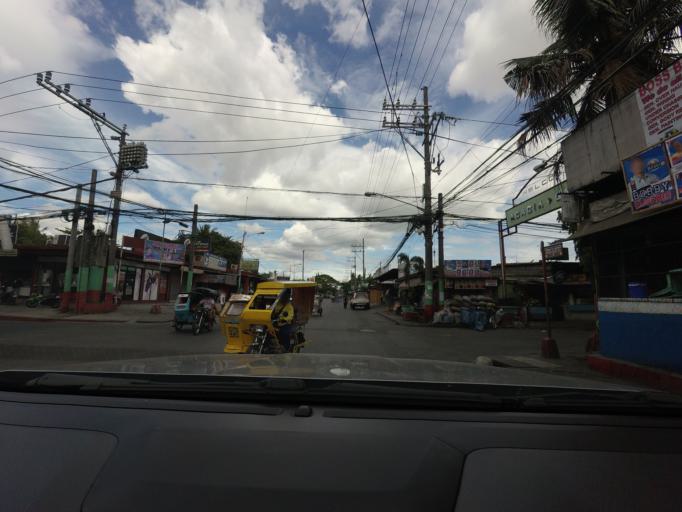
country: PH
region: Calabarzon
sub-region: Province of Rizal
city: Pateros
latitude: 14.5569
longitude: 121.0864
